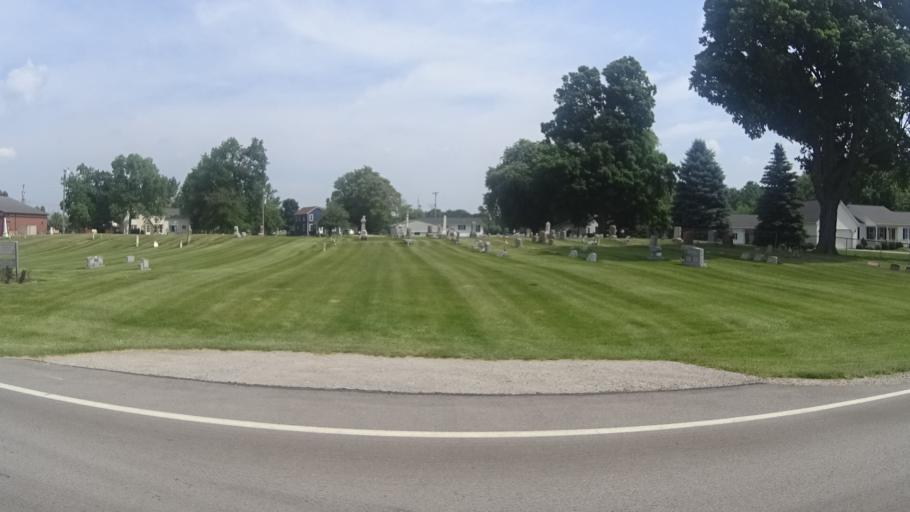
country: US
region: Ohio
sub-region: Erie County
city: Sandusky
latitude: 41.3550
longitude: -82.7231
